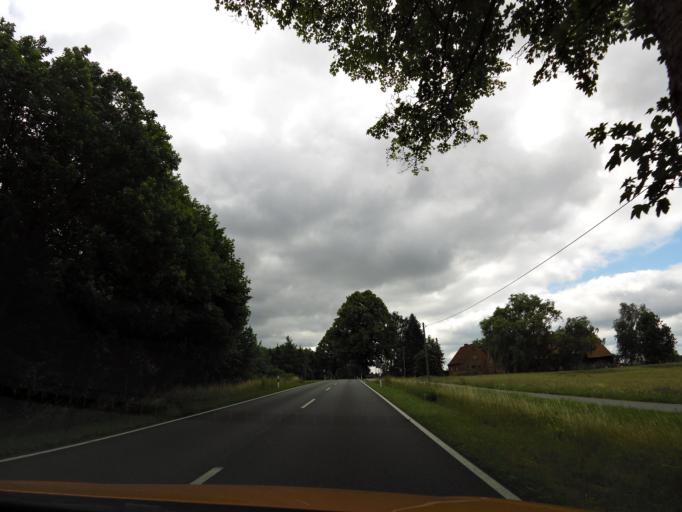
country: DE
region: Mecklenburg-Vorpommern
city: Muhl Rosin
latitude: 53.7419
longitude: 12.2636
